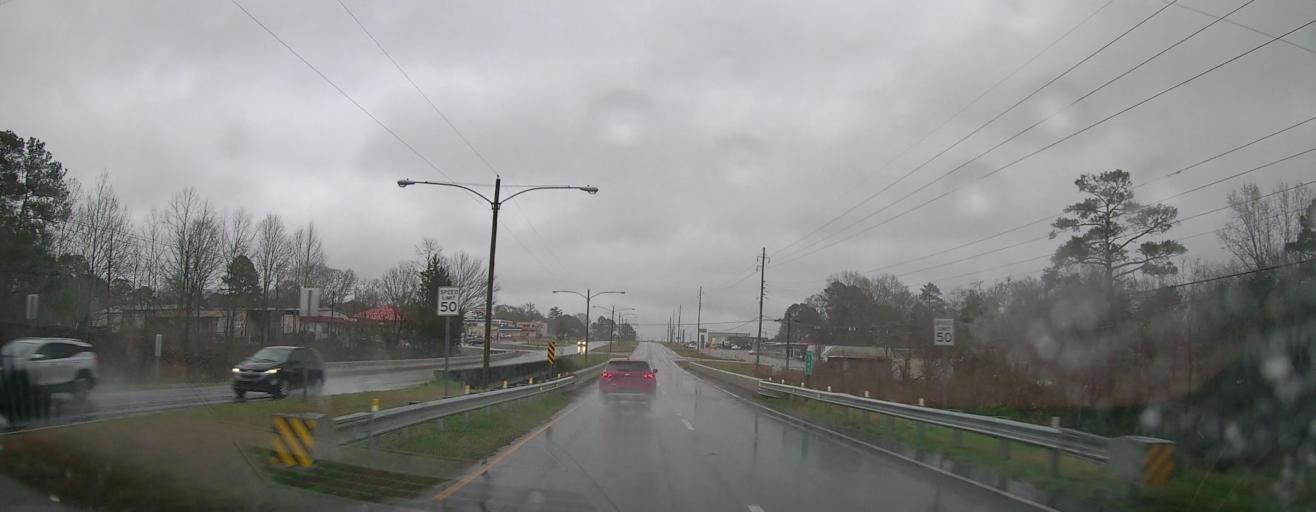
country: US
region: Alabama
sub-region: Morgan County
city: Hartselle
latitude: 34.4271
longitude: -86.9310
